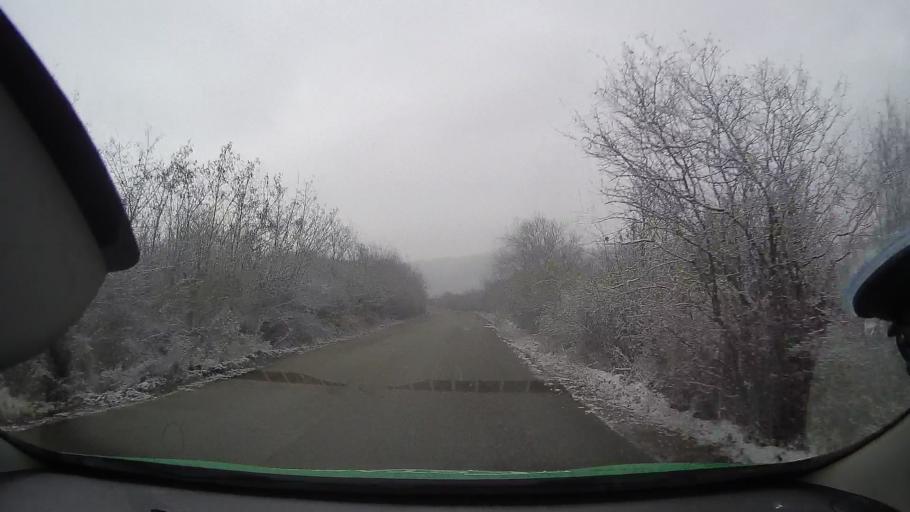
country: RO
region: Alba
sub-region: Comuna Hoparta
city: Hoparta
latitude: 46.3380
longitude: 23.9201
